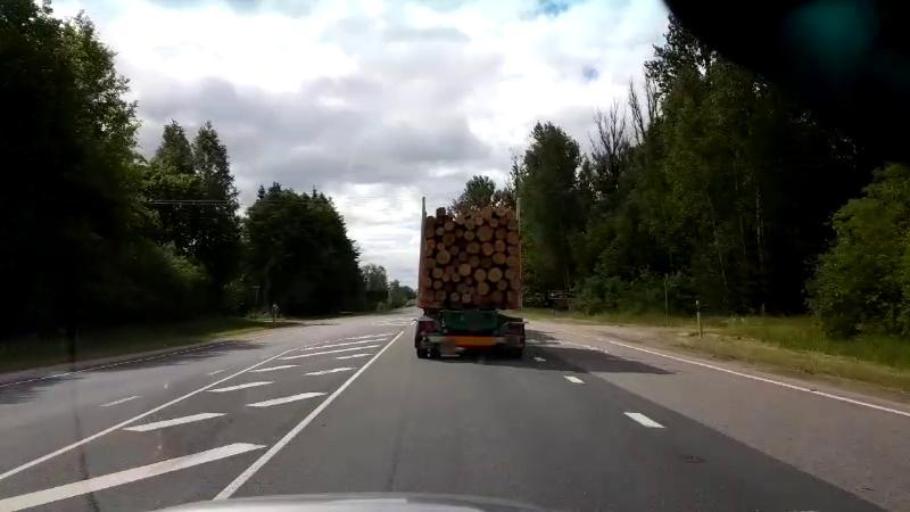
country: EE
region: Paernumaa
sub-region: Halinga vald
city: Parnu-Jaagupi
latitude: 58.6980
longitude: 24.4295
